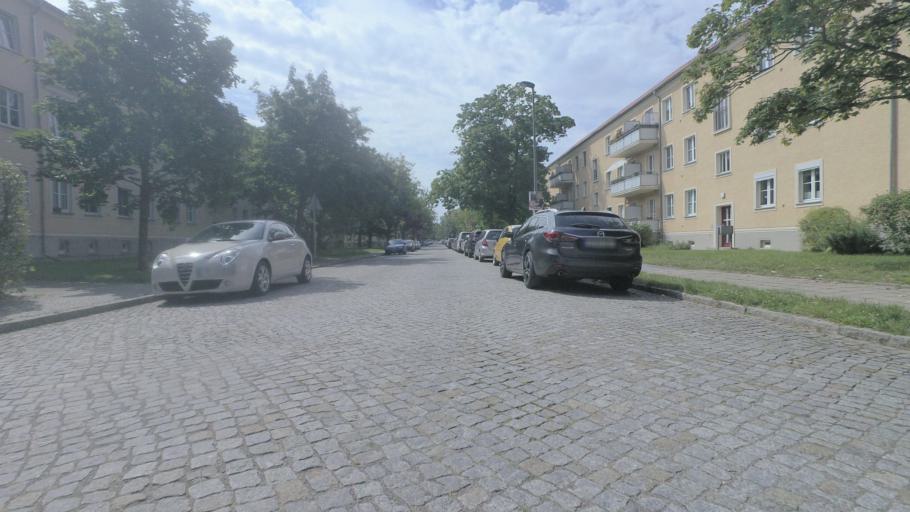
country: DE
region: Brandenburg
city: Ludwigsfelde
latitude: 52.3034
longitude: 13.2655
